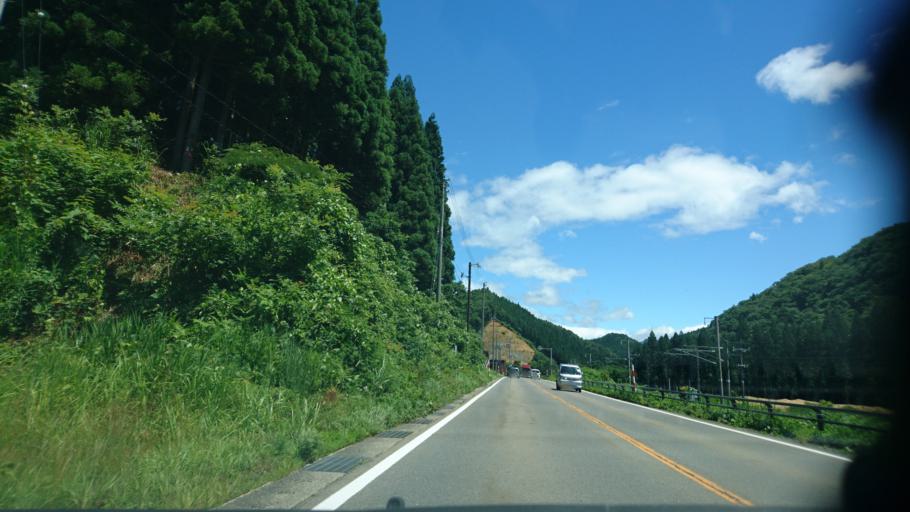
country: JP
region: Akita
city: Kakunodatemachi
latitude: 39.6482
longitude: 140.6654
